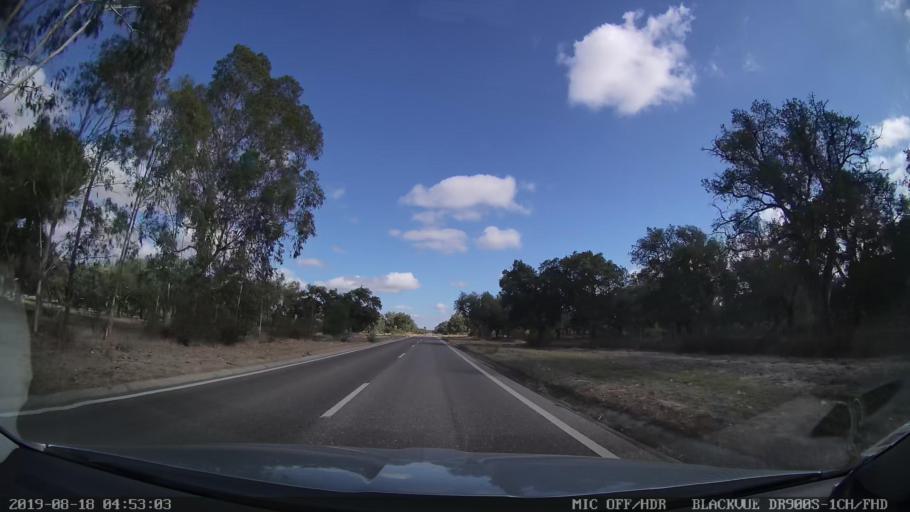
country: PT
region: Santarem
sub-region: Benavente
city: Poceirao
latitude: 38.9043
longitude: -8.7587
